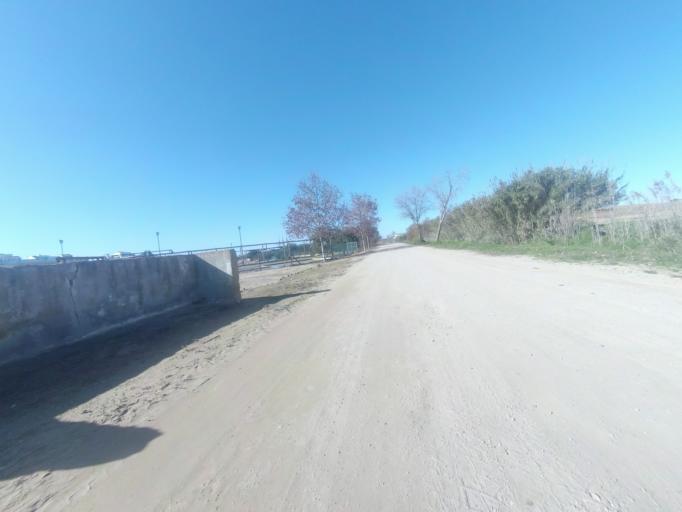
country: ES
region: Andalusia
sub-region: Provincia de Huelva
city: Palos de la Frontera
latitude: 37.2332
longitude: -6.8917
